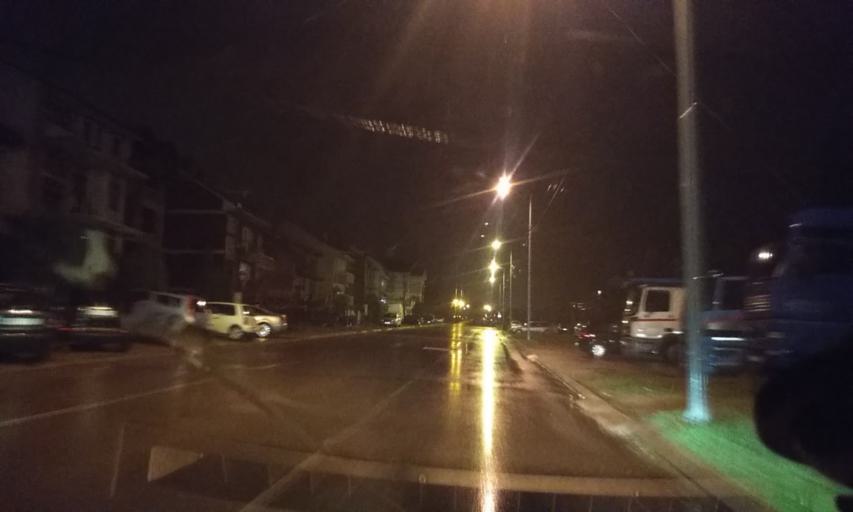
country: RS
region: Central Serbia
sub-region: Nisavski Okrug
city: Nis
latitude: 43.3102
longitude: 21.8600
